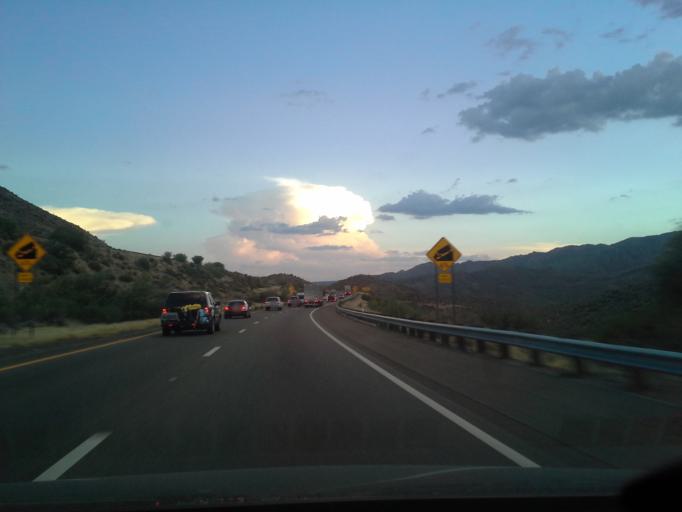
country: US
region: Arizona
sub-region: Yavapai County
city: Black Canyon City
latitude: 34.1333
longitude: -112.1489
